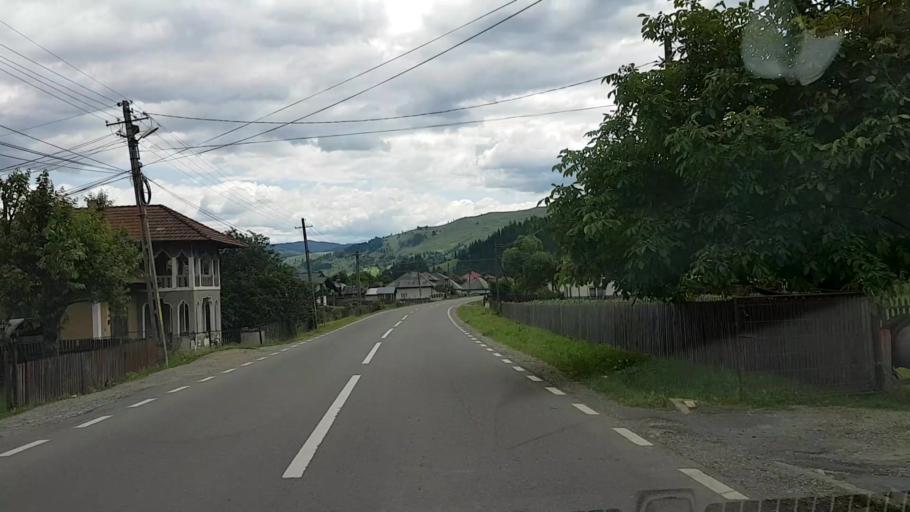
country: RO
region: Neamt
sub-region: Comuna Borca
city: Borca
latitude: 47.1900
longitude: 25.7720
